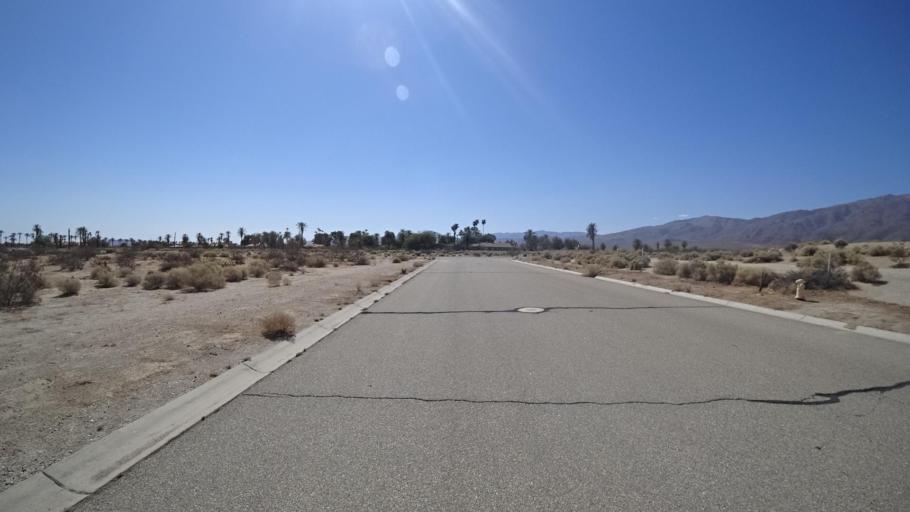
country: US
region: California
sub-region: San Diego County
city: Borrego Springs
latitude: 33.2361
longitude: -116.3592
